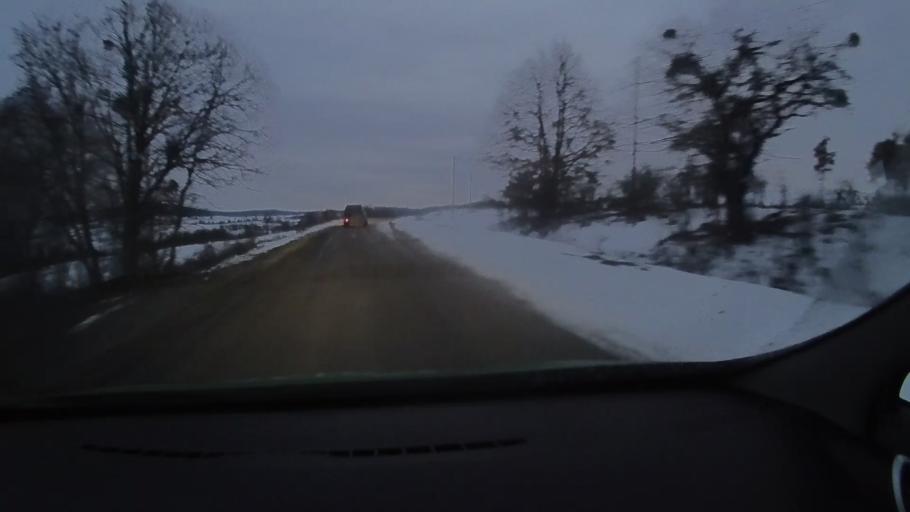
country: RO
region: Harghita
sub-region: Comuna Darjiu
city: Darjiu
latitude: 46.1917
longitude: 25.2463
